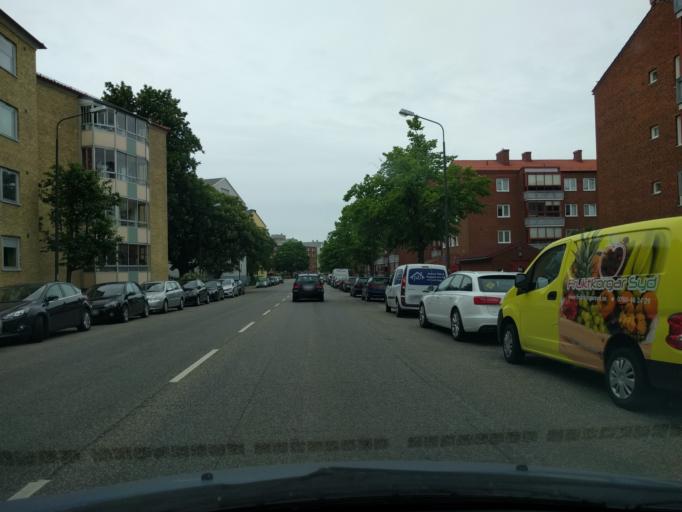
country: SE
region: Skane
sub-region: Malmo
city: Malmoe
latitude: 55.5914
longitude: 13.0277
